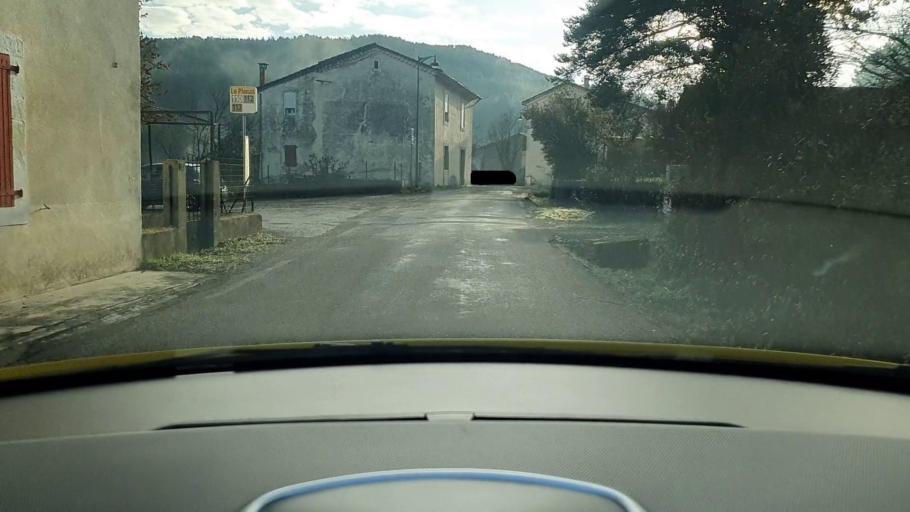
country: FR
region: Languedoc-Roussillon
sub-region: Departement du Gard
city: Branoux-les-Taillades
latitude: 44.2936
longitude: 4.0080
